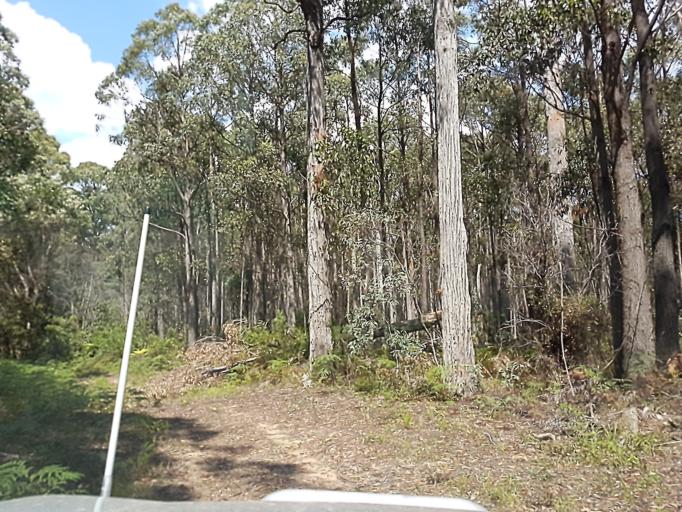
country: AU
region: Victoria
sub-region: East Gippsland
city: Lakes Entrance
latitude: -37.3260
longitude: 148.3261
